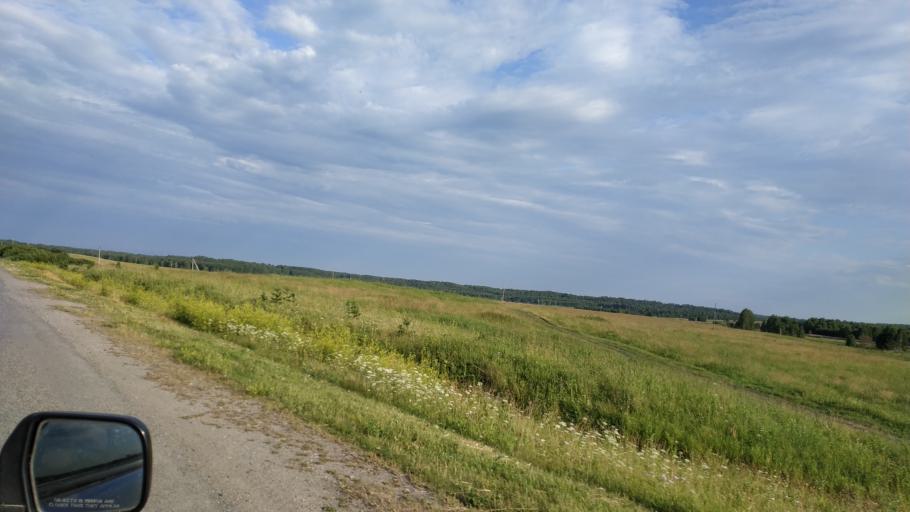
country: RU
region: Sverdlovsk
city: Yelanskiy
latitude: 57.0817
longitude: 62.4857
